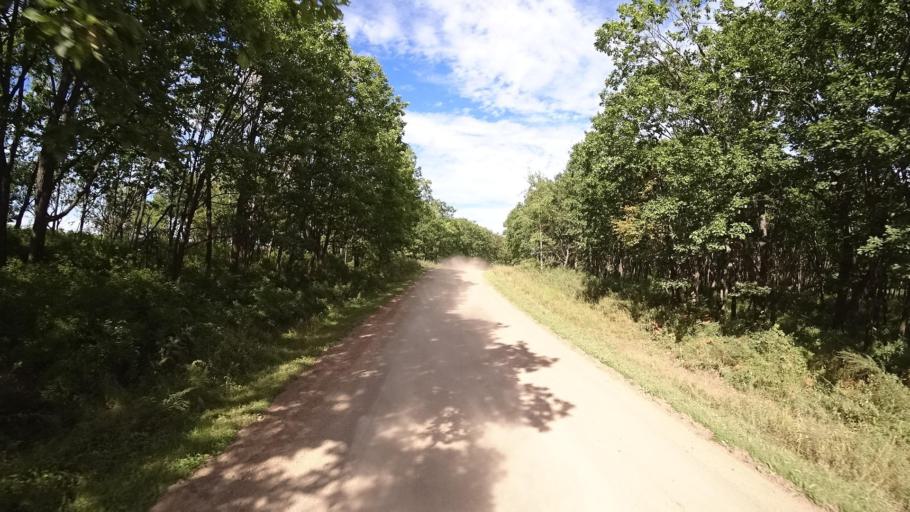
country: RU
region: Primorskiy
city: Yakovlevka
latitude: 44.4058
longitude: 133.5665
